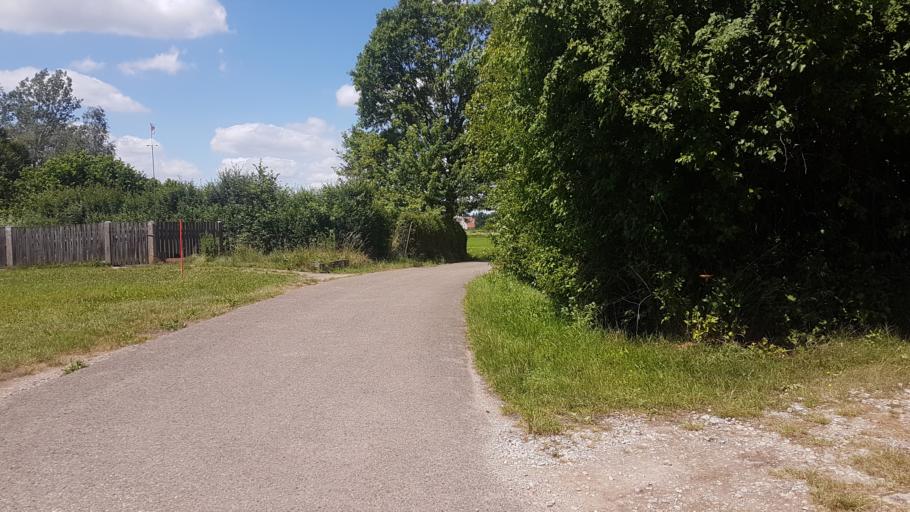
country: DE
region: Bavaria
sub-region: Regierungsbezirk Mittelfranken
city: Leutershausen
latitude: 49.3053
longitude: 10.4000
